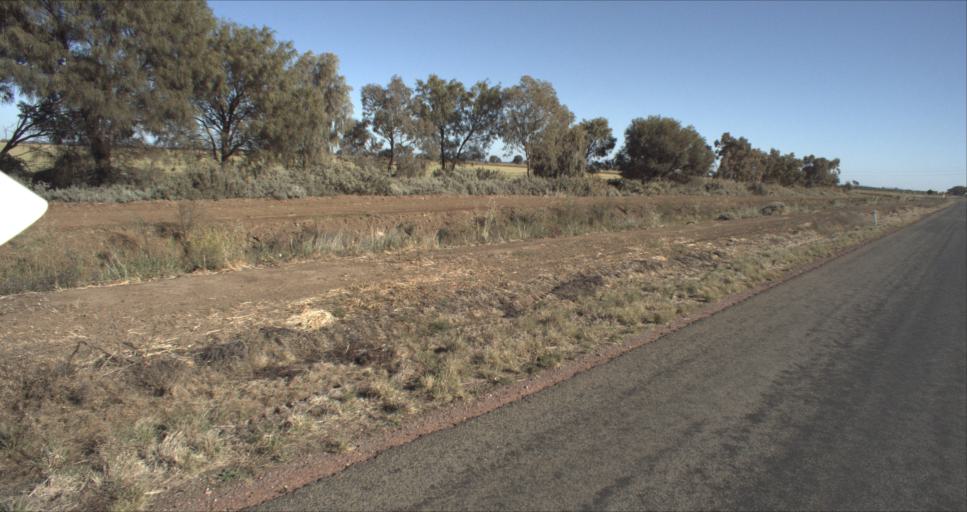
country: AU
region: New South Wales
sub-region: Leeton
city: Leeton
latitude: -34.5524
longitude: 146.2671
